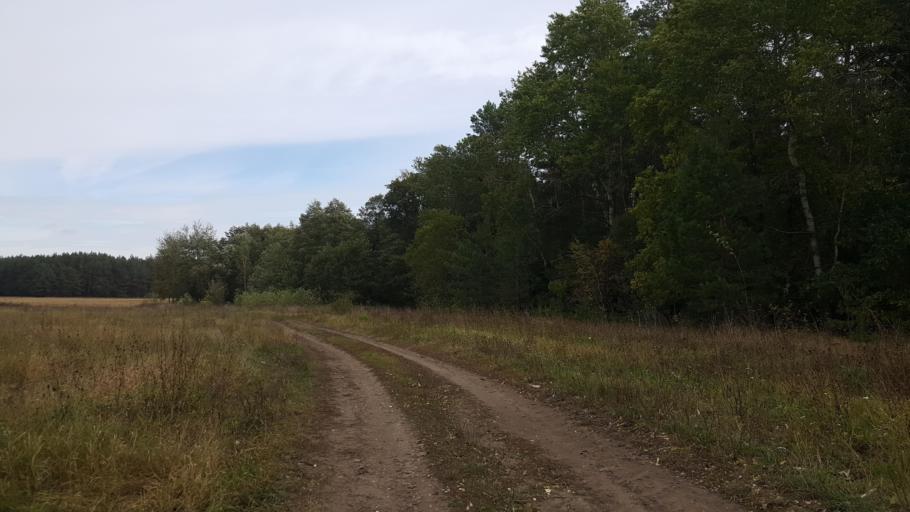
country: BY
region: Brest
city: Kamyanyets
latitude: 52.4229
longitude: 23.8942
